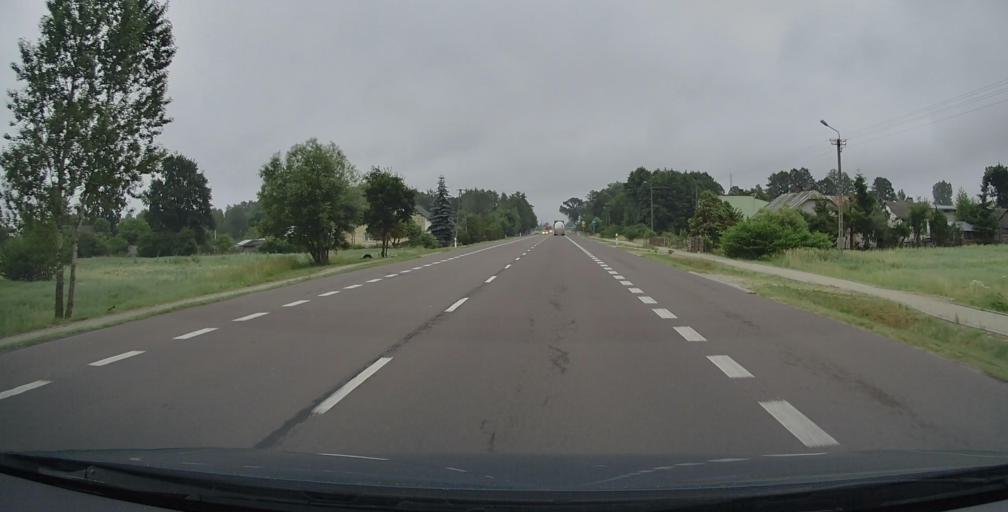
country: PL
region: Lublin Voivodeship
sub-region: Powiat bialski
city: Zalesie
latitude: 52.0370
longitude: 23.4636
